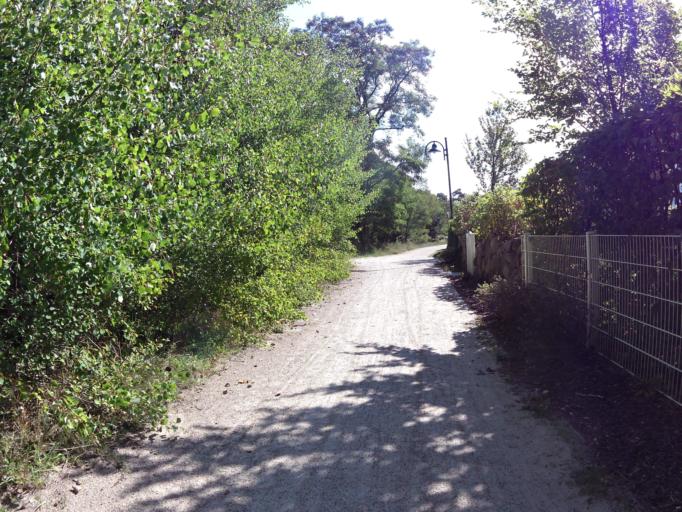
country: DE
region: Mecklenburg-Vorpommern
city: Karlshagen
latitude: 54.1287
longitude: 13.8341
